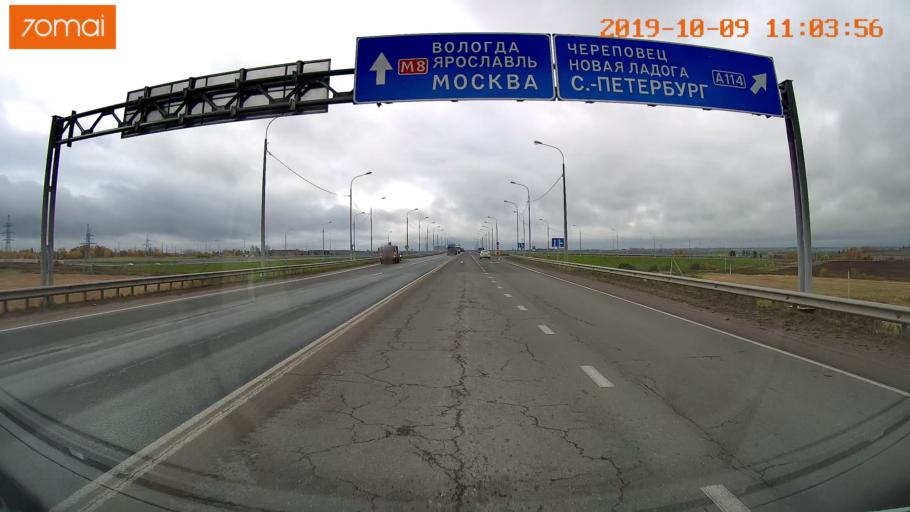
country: RU
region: Vologda
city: Vologda
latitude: 59.2172
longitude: 39.7726
